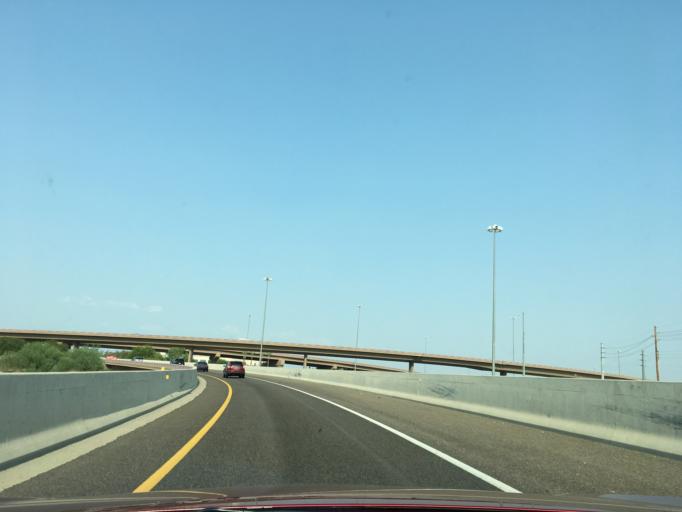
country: US
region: Arizona
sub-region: Maricopa County
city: Chandler
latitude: 33.2916
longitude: -111.8965
